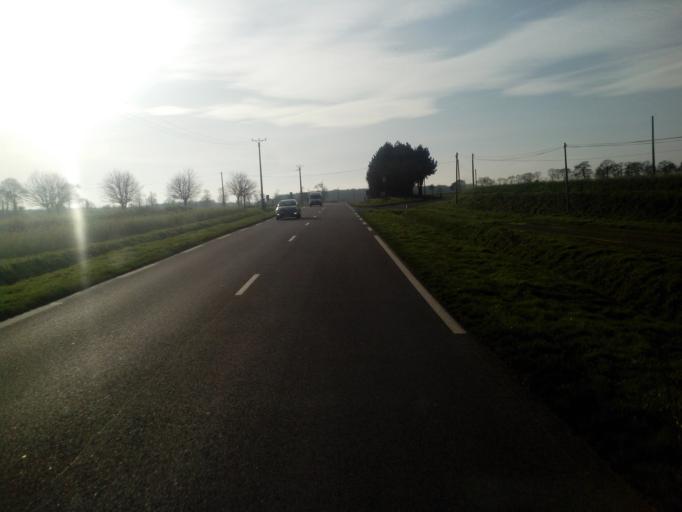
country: FR
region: Brittany
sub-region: Departement d'Ille-et-Vilaine
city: Gael
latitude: 48.1242
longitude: -2.2376
